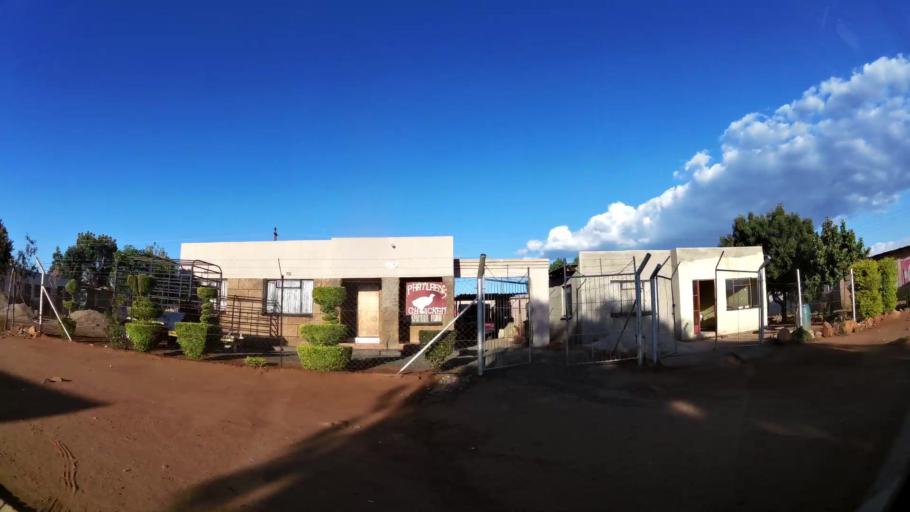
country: ZA
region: Limpopo
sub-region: Waterberg District Municipality
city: Mokopane
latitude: -24.1496
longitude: 28.9974
